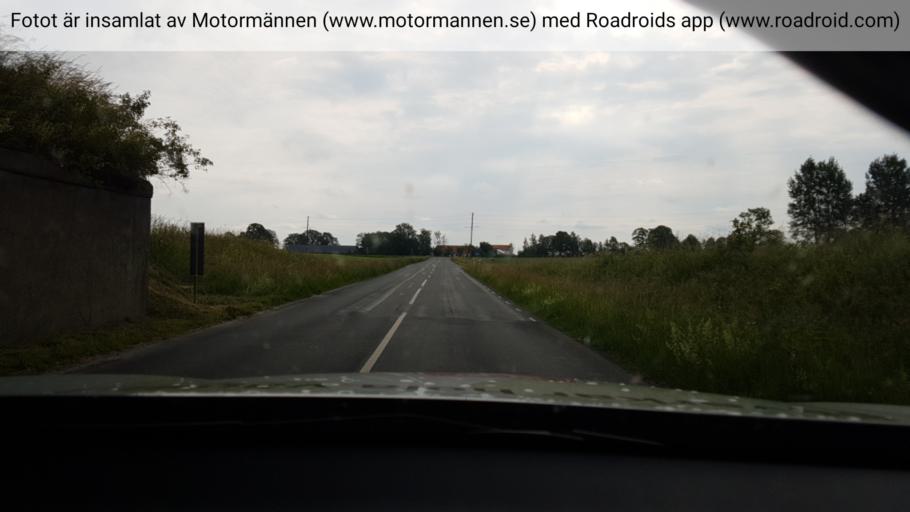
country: SE
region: Vaestra Goetaland
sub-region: Skovde Kommun
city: Skultorp
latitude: 58.3266
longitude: 13.8083
